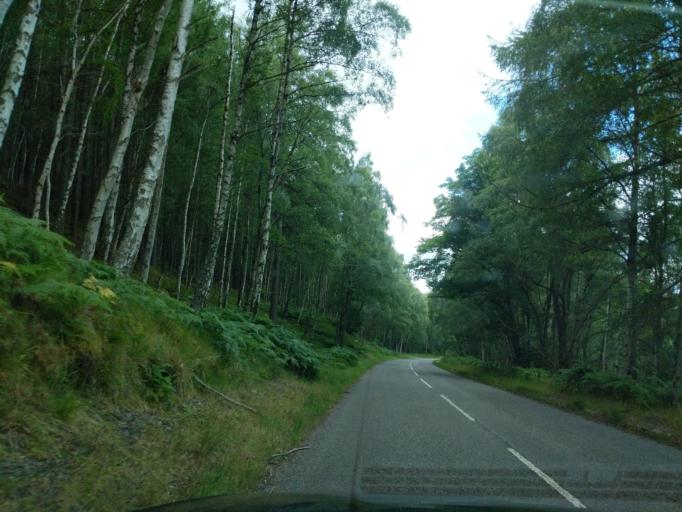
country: GB
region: Scotland
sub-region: Aberdeenshire
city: Ballater
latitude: 57.0555
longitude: -3.0095
